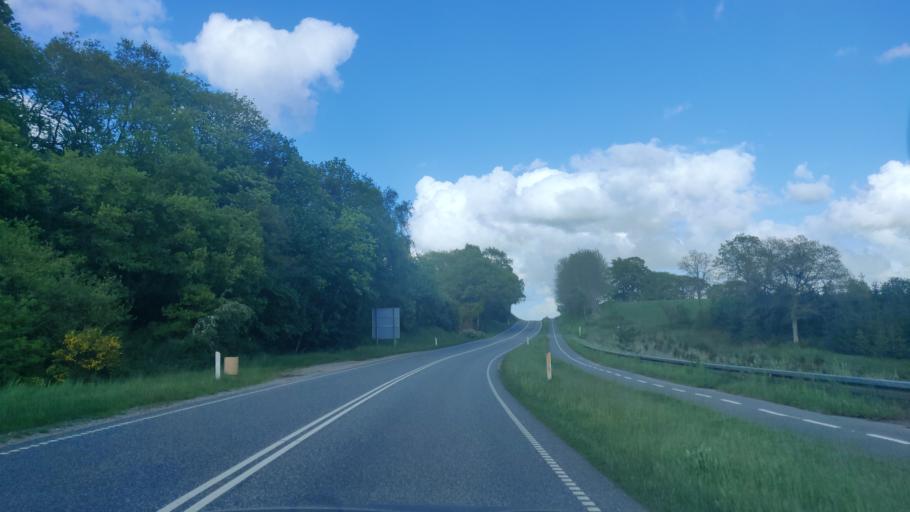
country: DK
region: Central Jutland
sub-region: Silkeborg Kommune
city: Kjellerup
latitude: 56.3547
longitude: 9.5295
